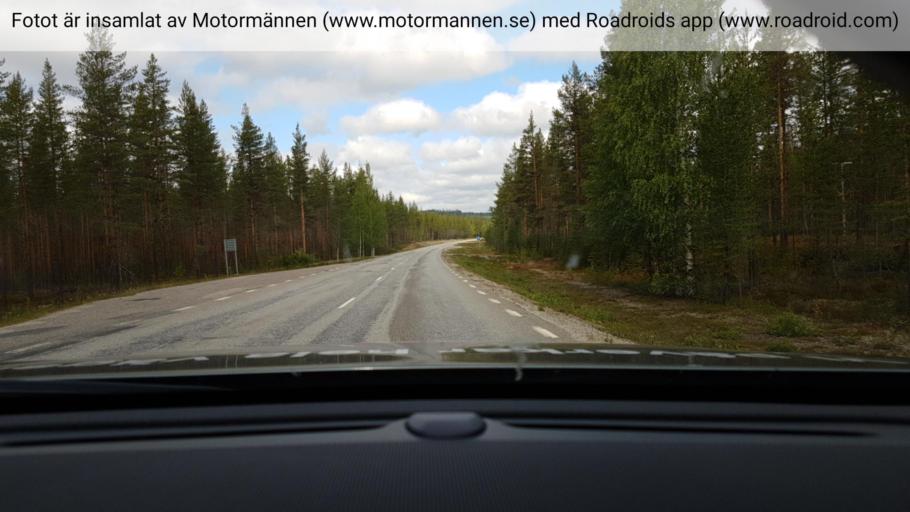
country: SE
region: Vaesterbotten
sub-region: Lycksele Kommun
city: Lycksele
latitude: 64.8574
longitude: 18.7332
